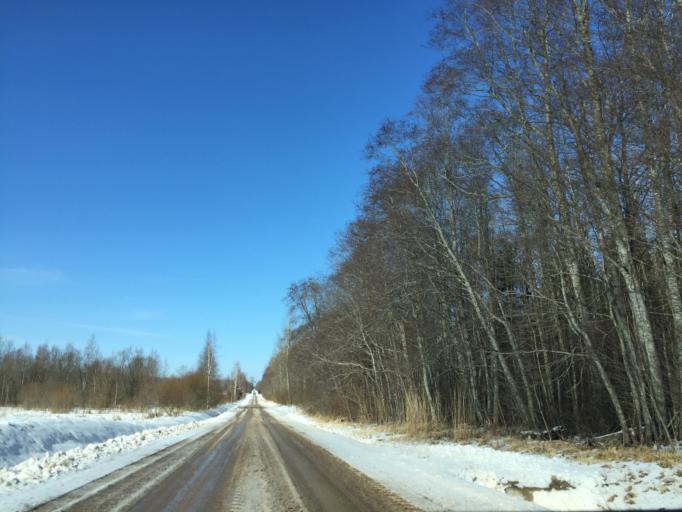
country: LV
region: Aloja
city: Staicele
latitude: 58.0262
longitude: 24.5844
